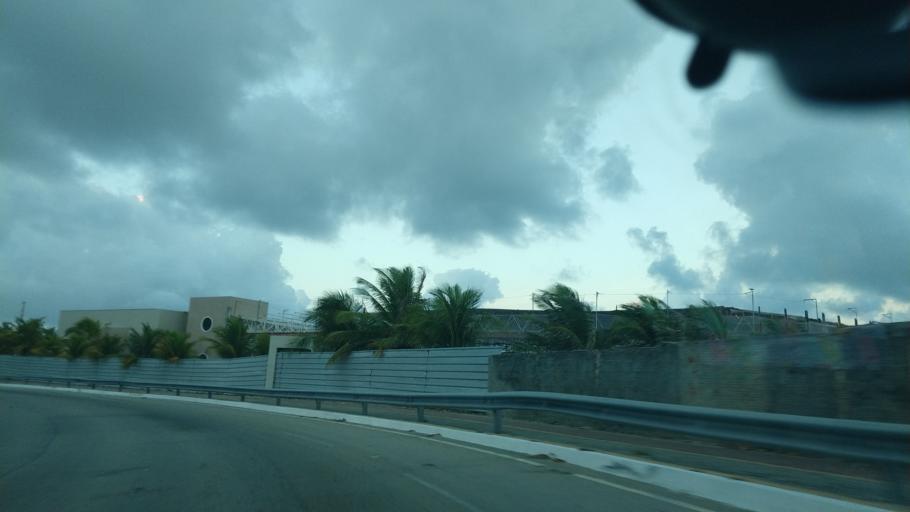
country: BR
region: Rio Grande do Norte
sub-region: Natal
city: Natal
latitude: -5.8053
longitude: -35.1819
